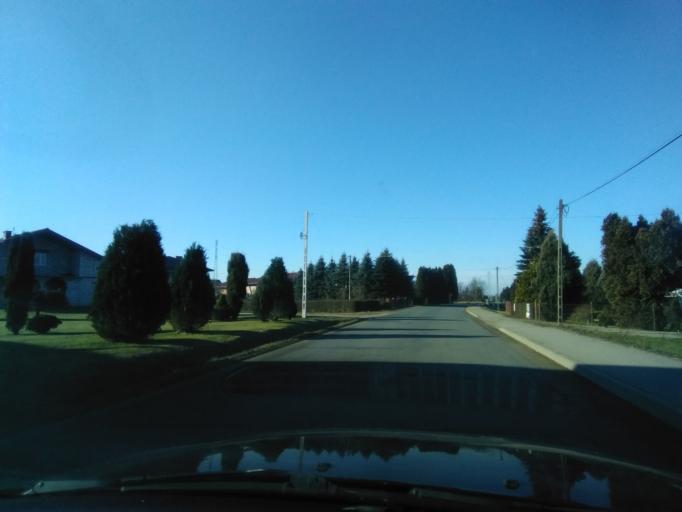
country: PL
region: Subcarpathian Voivodeship
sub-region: Powiat brzozowski
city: Haczow
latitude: 49.6741
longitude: 21.8862
